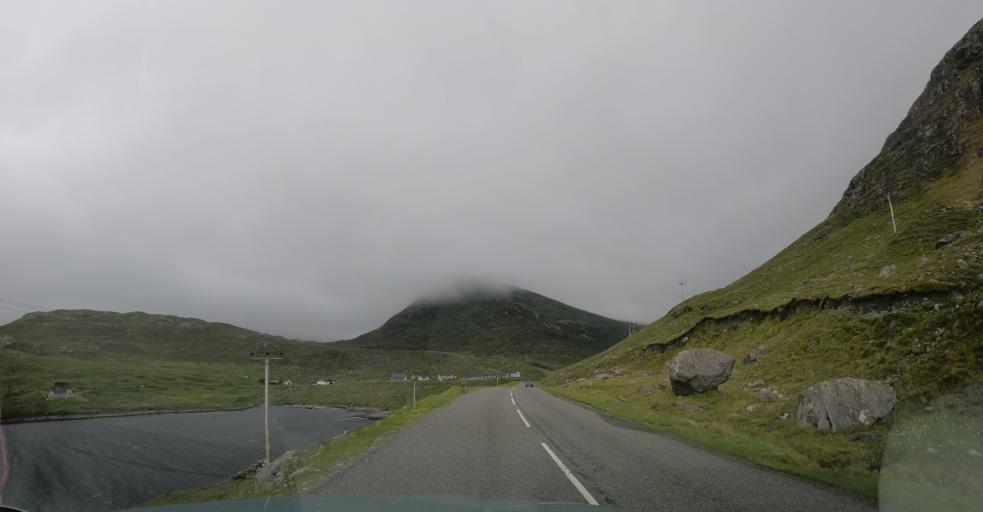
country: GB
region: Scotland
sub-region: Eilean Siar
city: Harris
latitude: 57.9266
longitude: -6.8434
